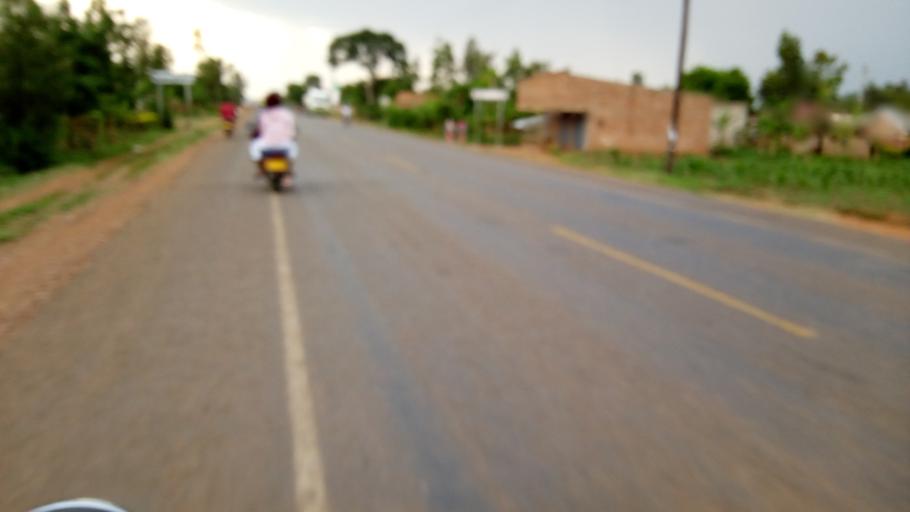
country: UG
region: Eastern Region
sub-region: Mbale District
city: Mbale
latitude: 1.1358
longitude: 34.1657
